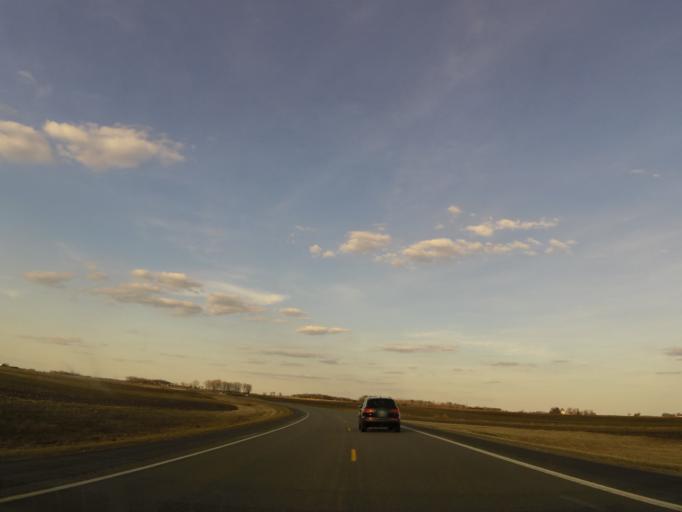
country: US
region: Minnesota
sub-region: McLeod County
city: Glencoe
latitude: 44.7332
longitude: -94.2947
